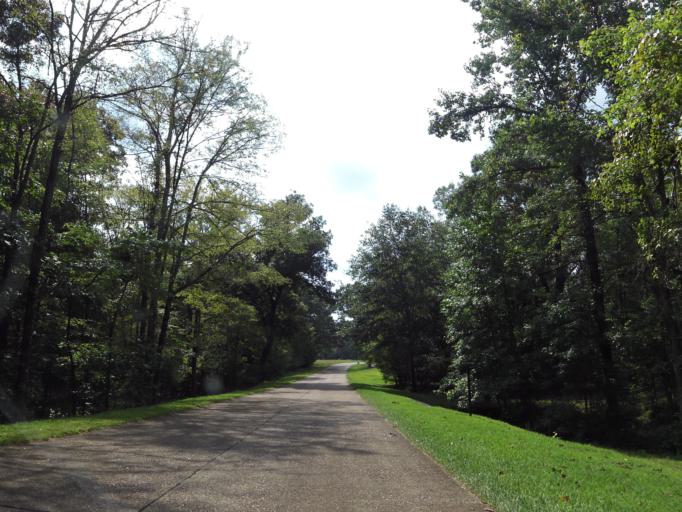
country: US
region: Tennessee
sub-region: Hardin County
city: Crump
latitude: 35.1387
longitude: -88.3383
